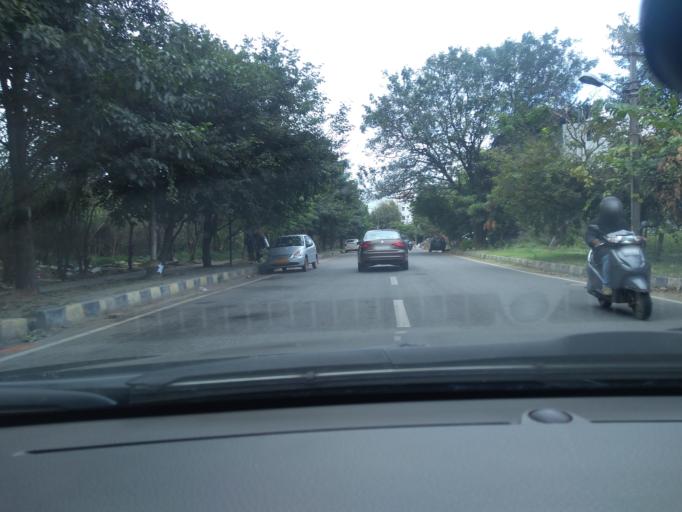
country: IN
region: Karnataka
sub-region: Bangalore Urban
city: Bangalore
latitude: 12.9982
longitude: 77.6623
